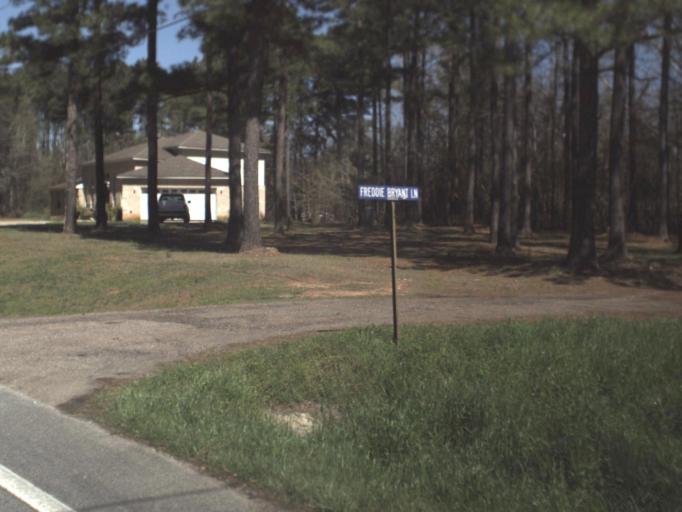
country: US
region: Florida
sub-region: Gadsden County
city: Quincy
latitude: 30.6214
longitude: -84.5944
